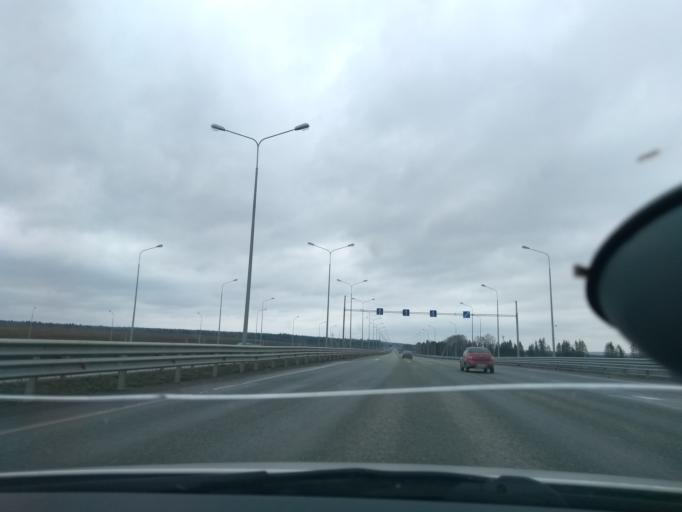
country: RU
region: Perm
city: Bershet'
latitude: 57.6826
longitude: 56.4245
